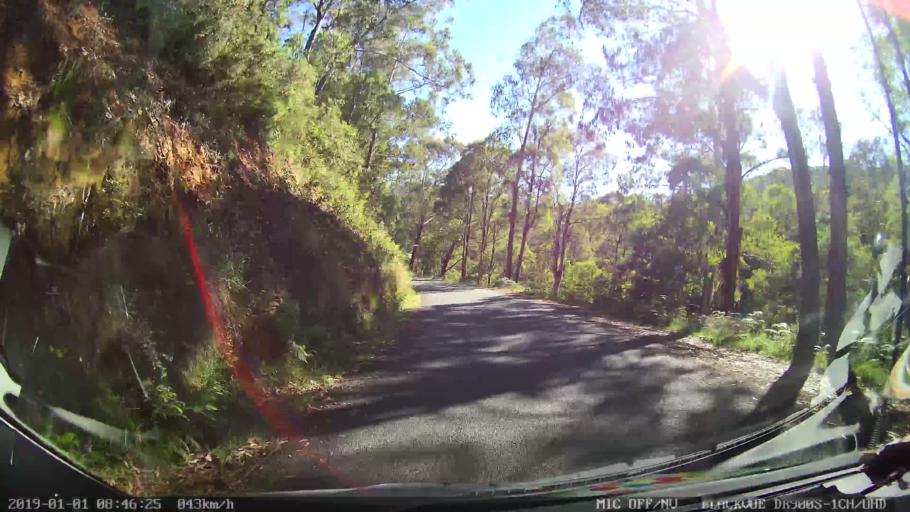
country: AU
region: New South Wales
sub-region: Snowy River
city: Jindabyne
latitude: -36.3003
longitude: 148.1932
